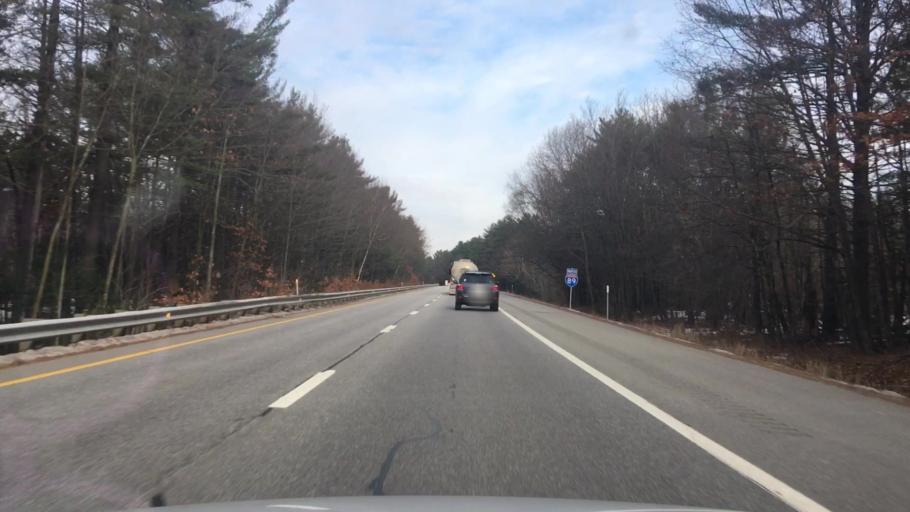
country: US
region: New Hampshire
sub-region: Merrimack County
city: Contoocook
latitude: 43.2082
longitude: -71.7117
